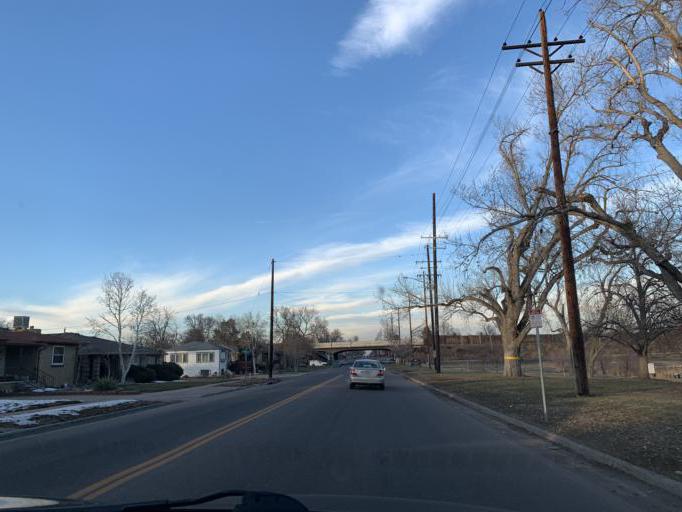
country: US
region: Colorado
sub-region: Adams County
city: Berkley
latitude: 39.7814
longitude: -105.0346
